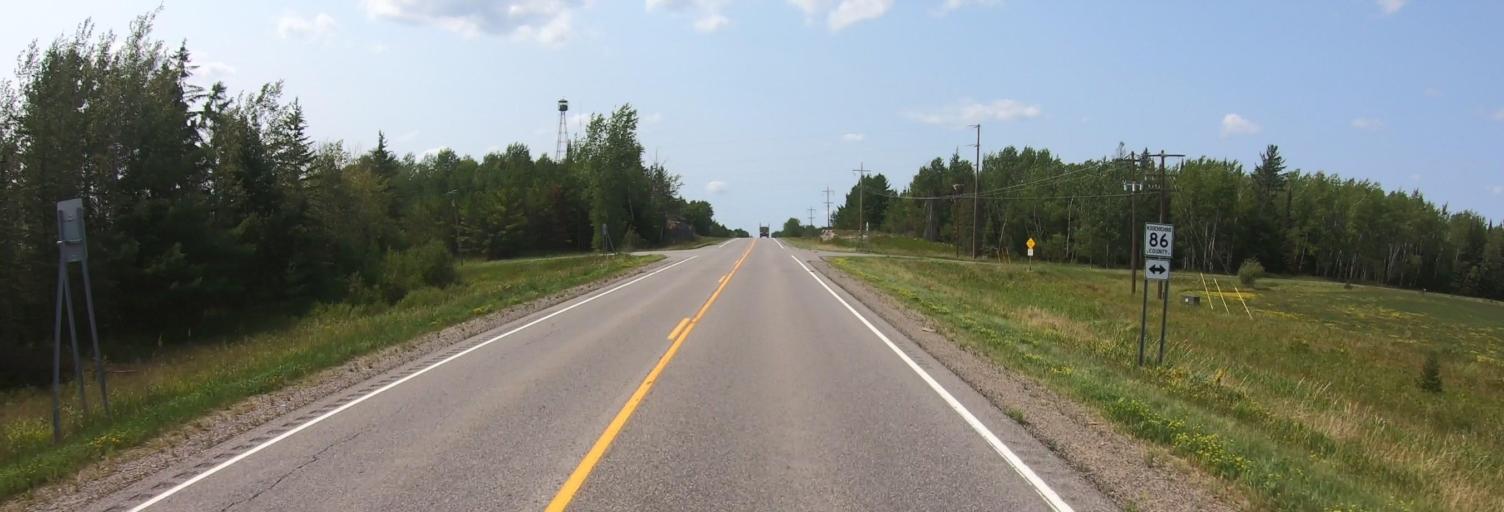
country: US
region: Minnesota
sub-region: Lake of the Woods County
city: Baudette
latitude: 48.6273
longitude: -94.0784
